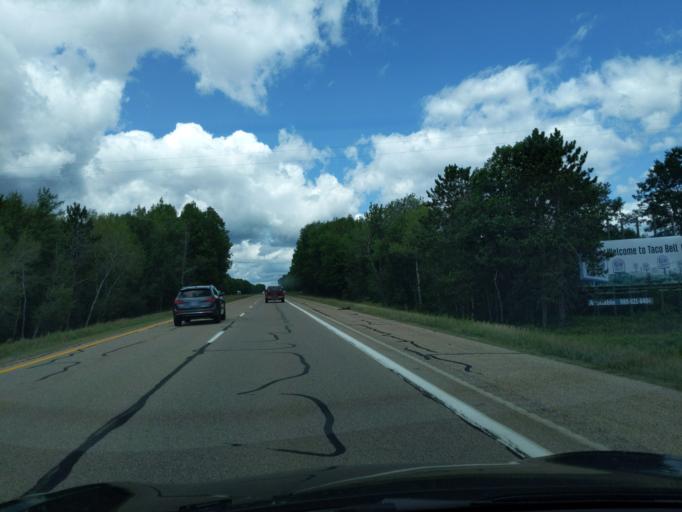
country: US
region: Michigan
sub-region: Roscommon County
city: Houghton Lake
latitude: 44.3200
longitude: -84.8064
